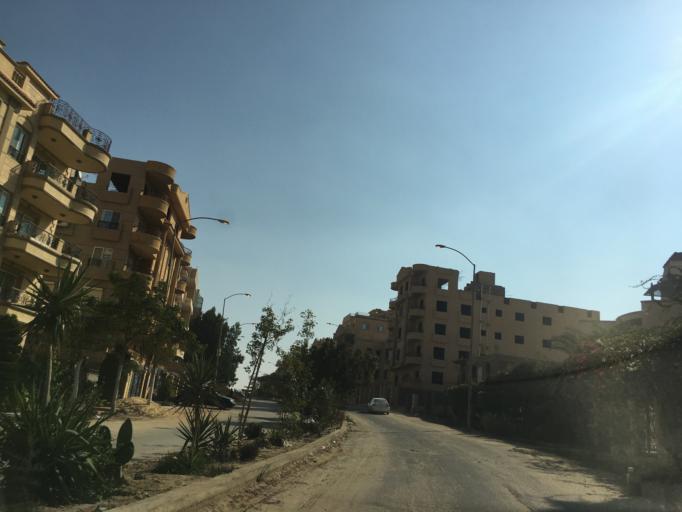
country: EG
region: Al Jizah
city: Awsim
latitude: 29.9995
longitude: 30.9871
